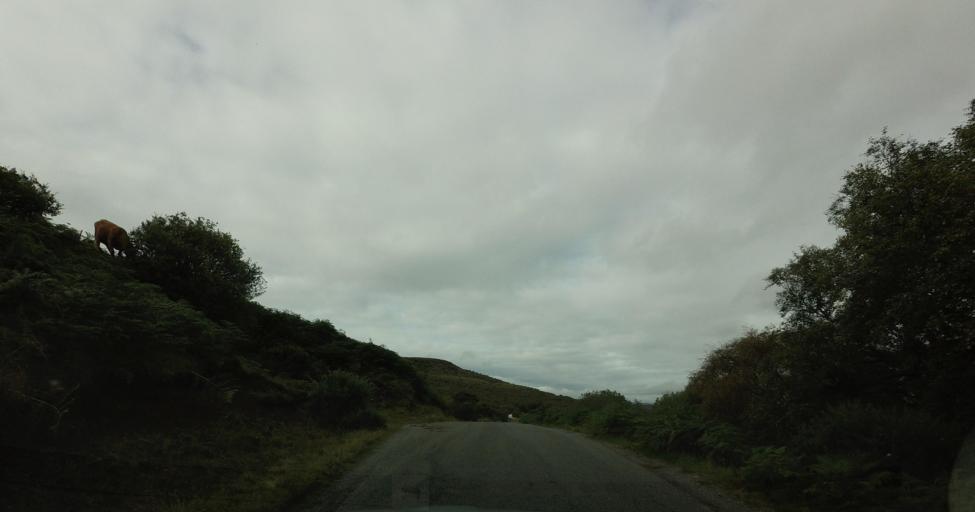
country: GB
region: Scotland
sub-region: Highland
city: Portree
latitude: 57.4172
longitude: -6.2300
